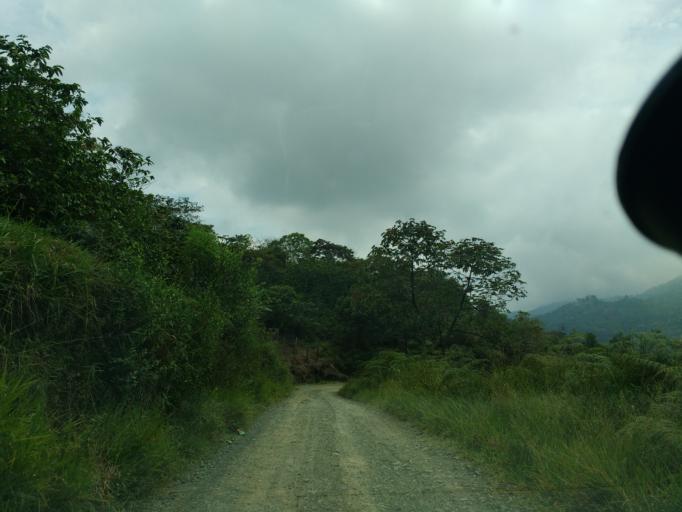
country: CO
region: Cauca
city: Santander de Quilichao
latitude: 2.9188
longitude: -76.4743
